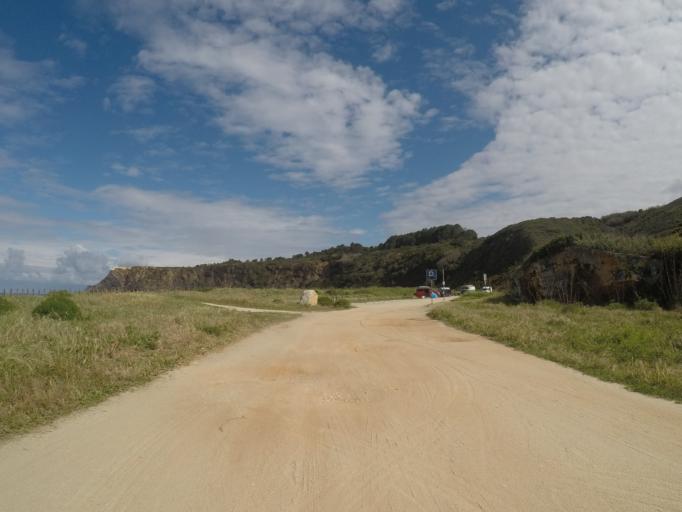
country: PT
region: Beja
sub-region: Odemira
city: Sao Teotonio
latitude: 37.4404
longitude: -8.7953
